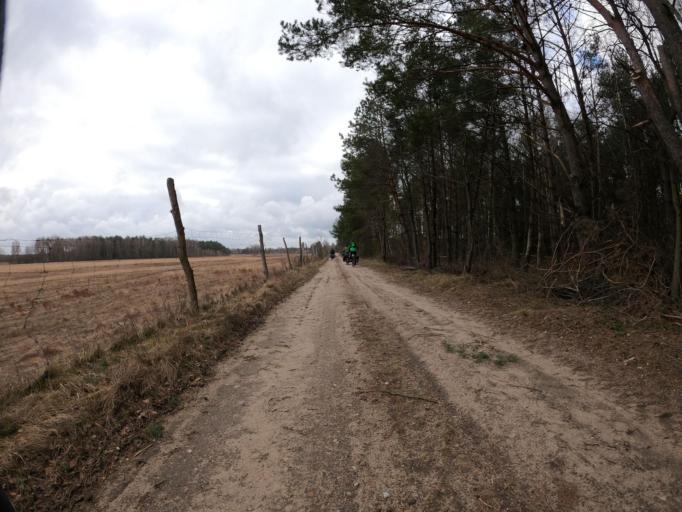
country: PL
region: Greater Poland Voivodeship
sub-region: Powiat zlotowski
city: Sypniewo
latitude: 53.4742
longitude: 16.5103
